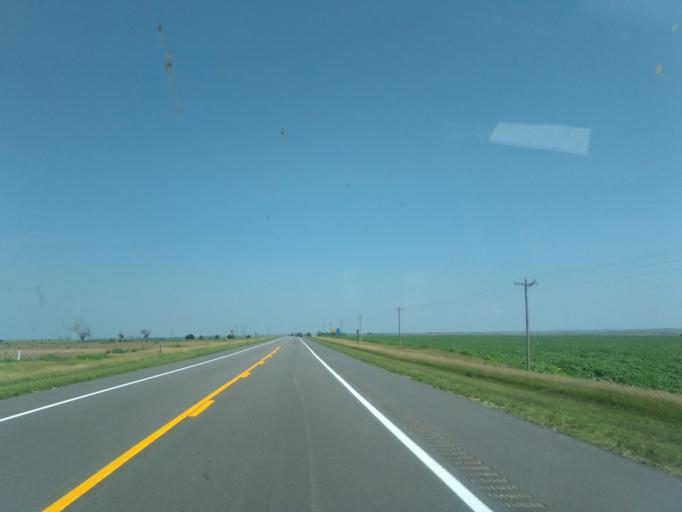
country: US
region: Nebraska
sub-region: Red Willow County
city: McCook
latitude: 40.3144
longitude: -100.6494
